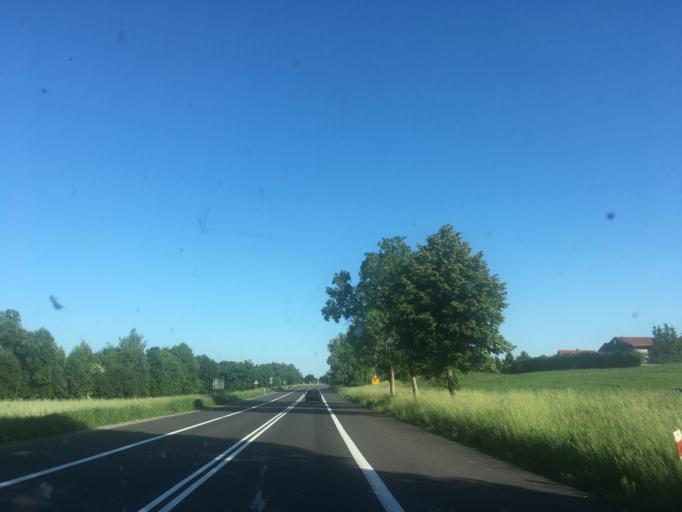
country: PL
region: Warmian-Masurian Voivodeship
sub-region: Powiat ostrodzki
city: Ostroda
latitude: 53.6708
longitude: 20.0350
